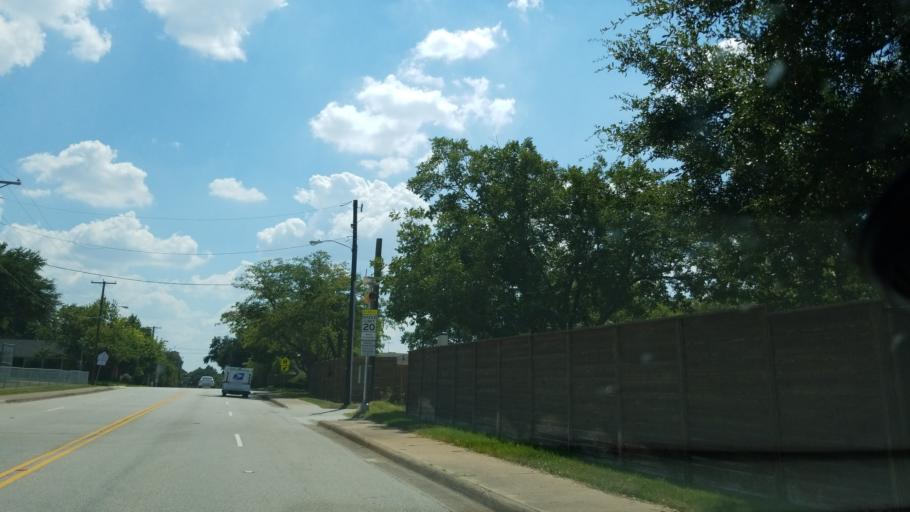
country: US
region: Texas
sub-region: Dallas County
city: Richardson
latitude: 32.8838
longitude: -96.7092
